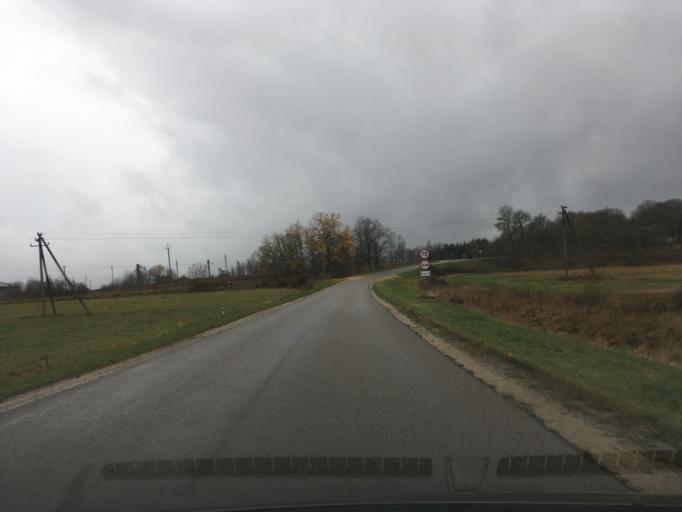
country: EE
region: Laeaene
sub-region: Lihula vald
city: Lihula
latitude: 58.6940
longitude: 23.8472
